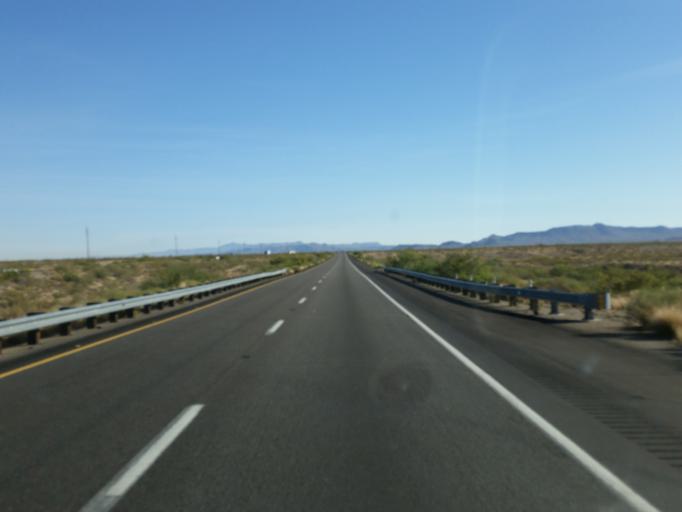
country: US
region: Arizona
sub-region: Mohave County
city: Kingman
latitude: 34.9814
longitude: -114.1398
